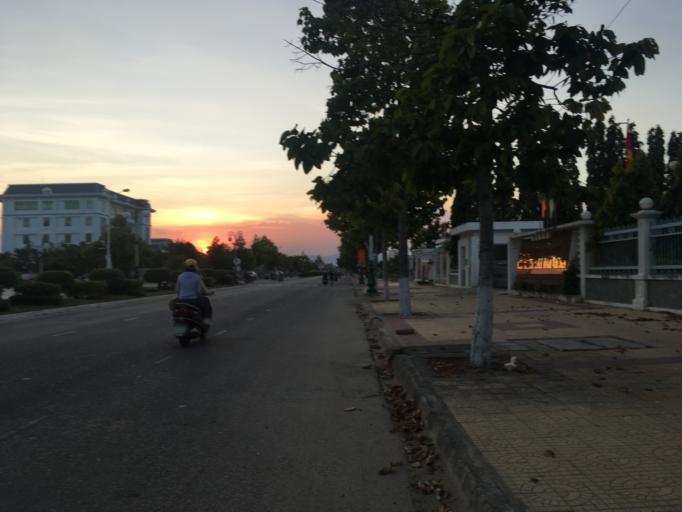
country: VN
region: Ninh Thuan
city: Phan Rang-Thap Cham
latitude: 11.5641
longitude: 109.0096
